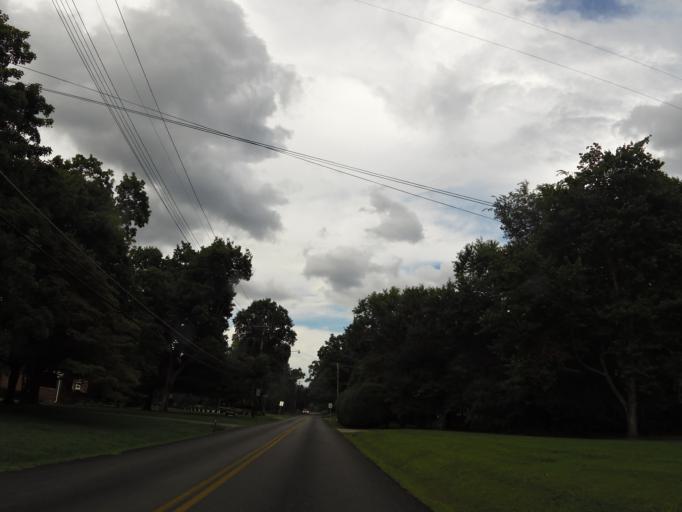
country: US
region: Kentucky
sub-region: Christian County
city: Hopkinsville
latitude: 36.8504
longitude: -87.5080
